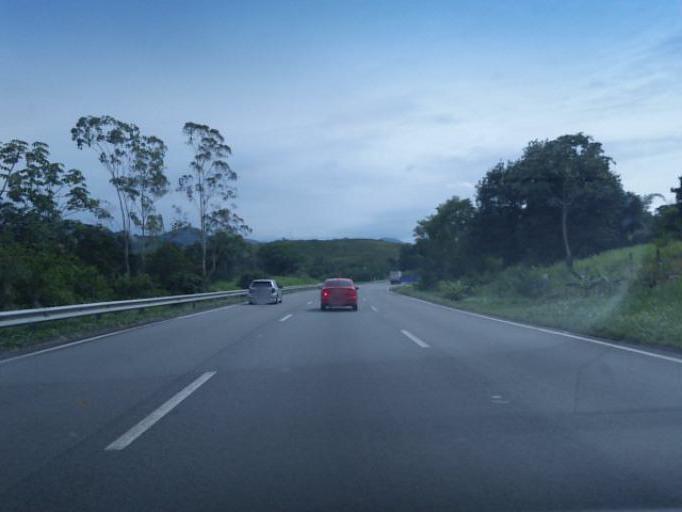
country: BR
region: Sao Paulo
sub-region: Cajati
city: Cajati
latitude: -24.7790
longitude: -48.1732
